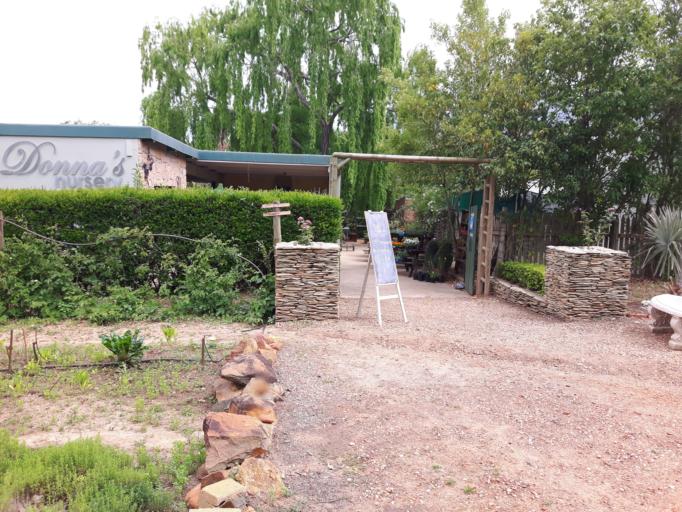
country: ZA
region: Western Cape
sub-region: Overberg District Municipality
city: Swellendam
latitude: -34.0193
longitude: 20.4524
